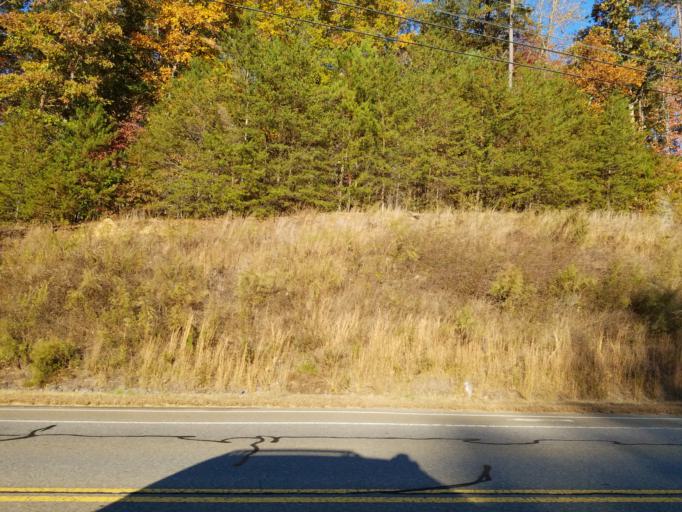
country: US
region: Georgia
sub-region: Gilmer County
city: Ellijay
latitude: 34.6649
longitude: -84.4505
